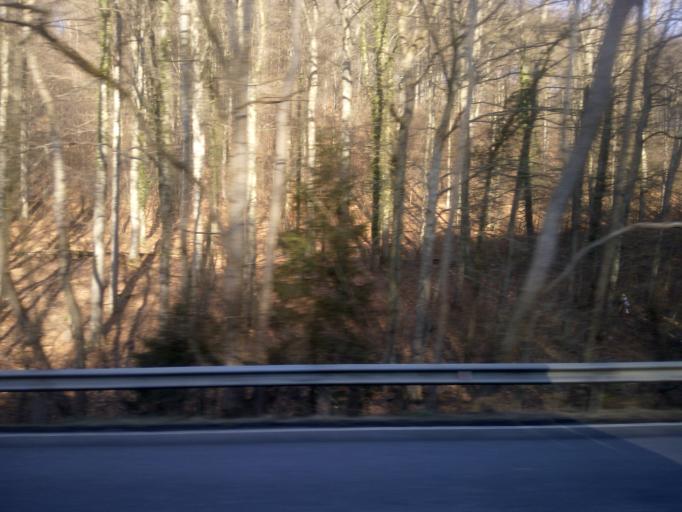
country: LU
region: Luxembourg
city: Kirchberg
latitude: 49.6425
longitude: 6.1628
